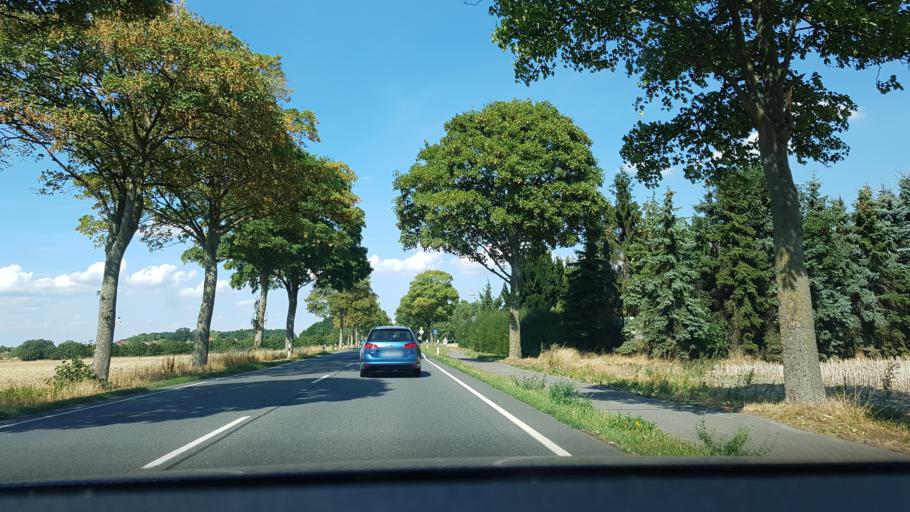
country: DE
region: Lower Saxony
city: Rotgesbuttel
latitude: 52.4089
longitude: 10.5280
